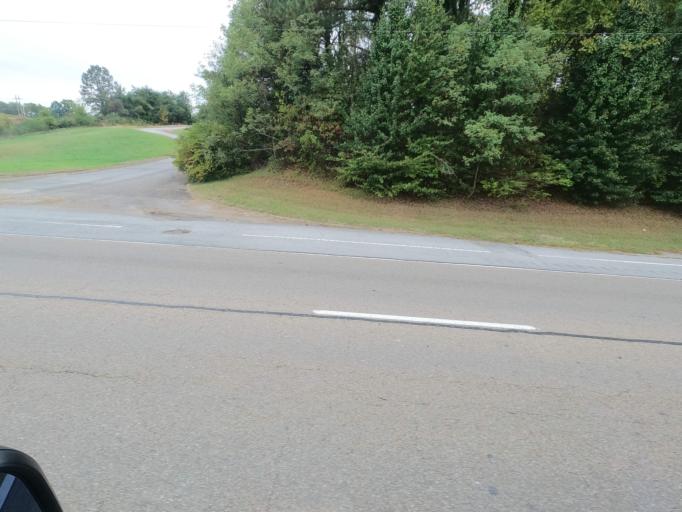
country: US
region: Tennessee
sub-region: Hawkins County
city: Mount Carmel
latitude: 36.5531
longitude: -82.6202
